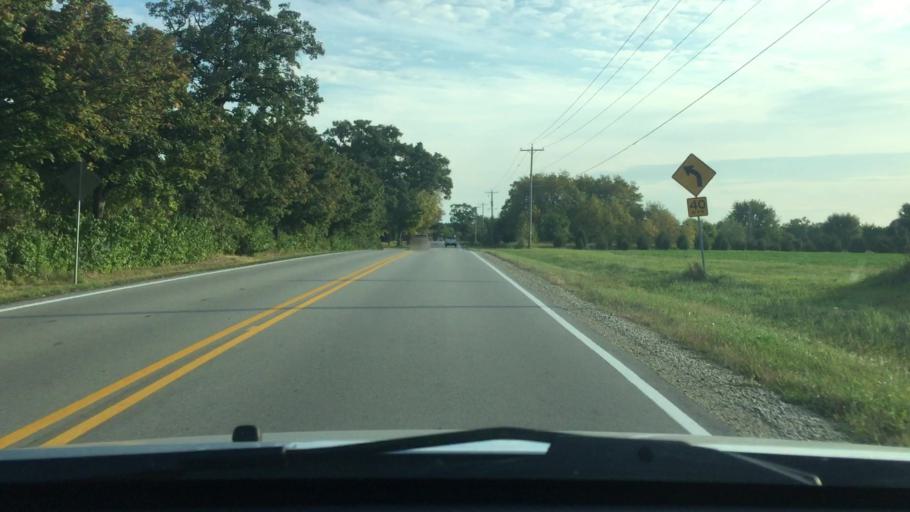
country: US
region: Wisconsin
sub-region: Waukesha County
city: Wales
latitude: 42.9760
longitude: -88.3963
